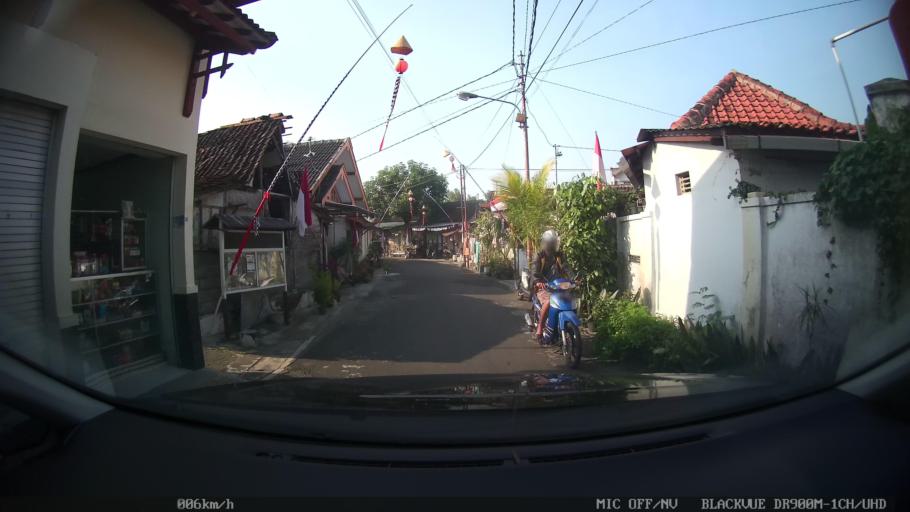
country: ID
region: Daerah Istimewa Yogyakarta
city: Yogyakarta
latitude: -7.8092
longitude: 110.3647
